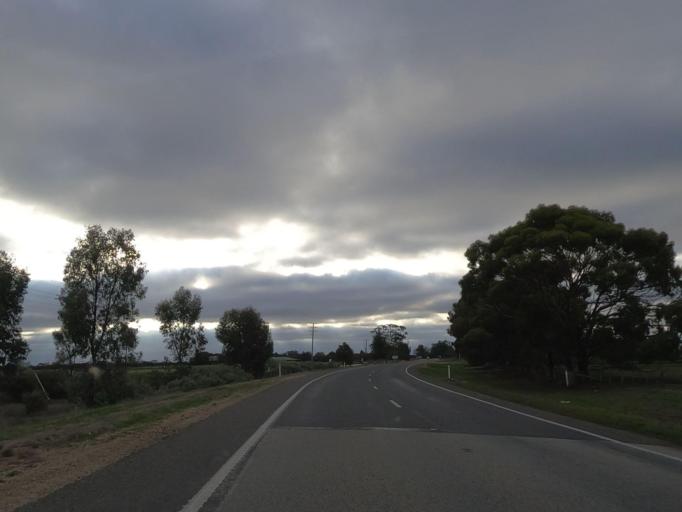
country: AU
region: Victoria
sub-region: Swan Hill
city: Swan Hill
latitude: -35.7281
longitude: 143.8921
